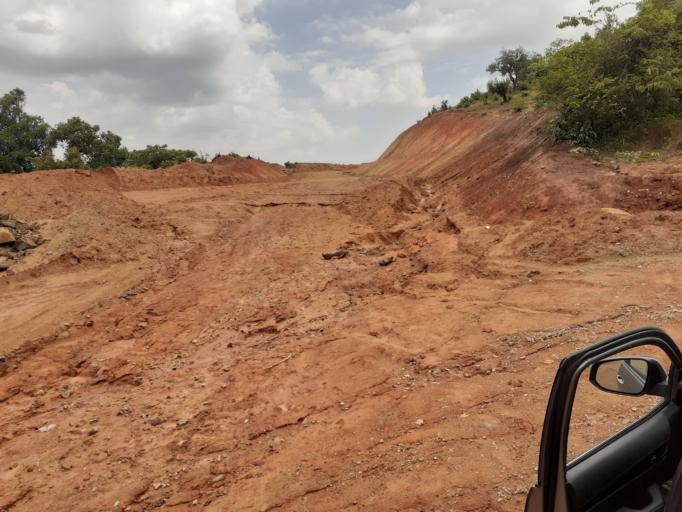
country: ET
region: Oromiya
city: Gimbi
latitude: 9.3216
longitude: 35.6928
